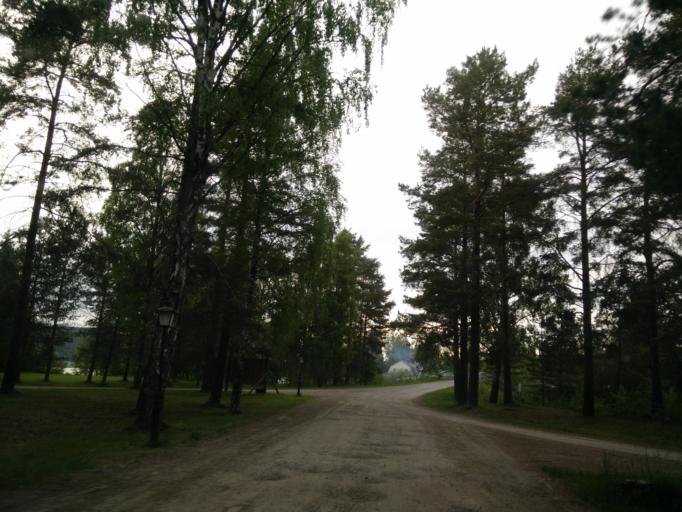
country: SE
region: Vaesternorrland
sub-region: Kramfors Kommun
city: Kramfors
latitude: 63.0102
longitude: 17.7958
